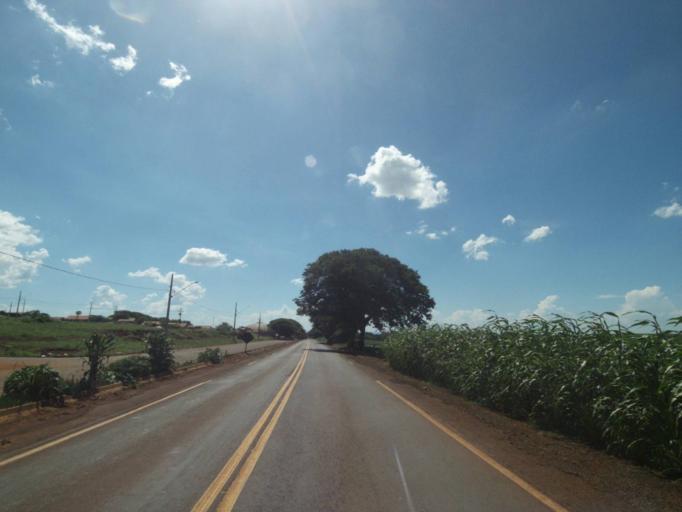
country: BR
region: Parana
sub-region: Sertanopolis
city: Sertanopolis
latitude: -23.0346
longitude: -50.8095
